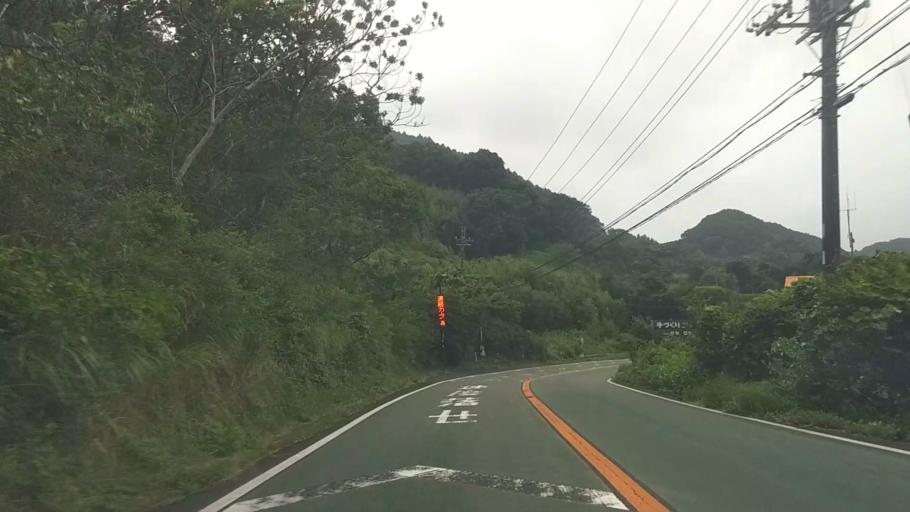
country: JP
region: Chiba
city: Tateyama
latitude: 35.1407
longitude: 139.9119
